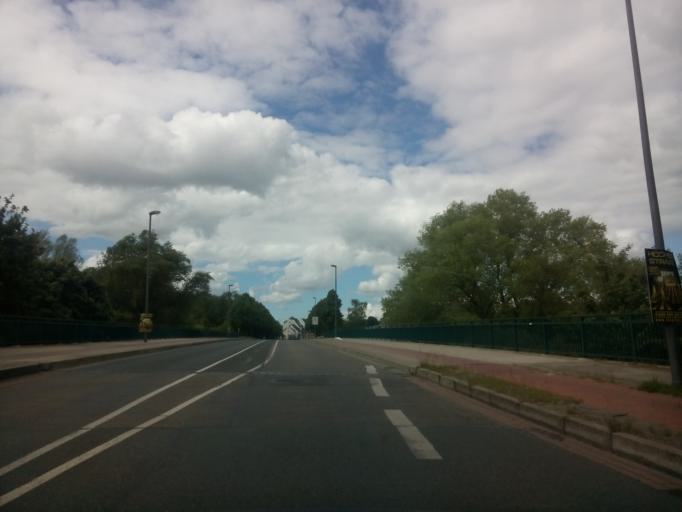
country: DE
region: Lower Saxony
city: Ritterhude
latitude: 53.1638
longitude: 8.7029
